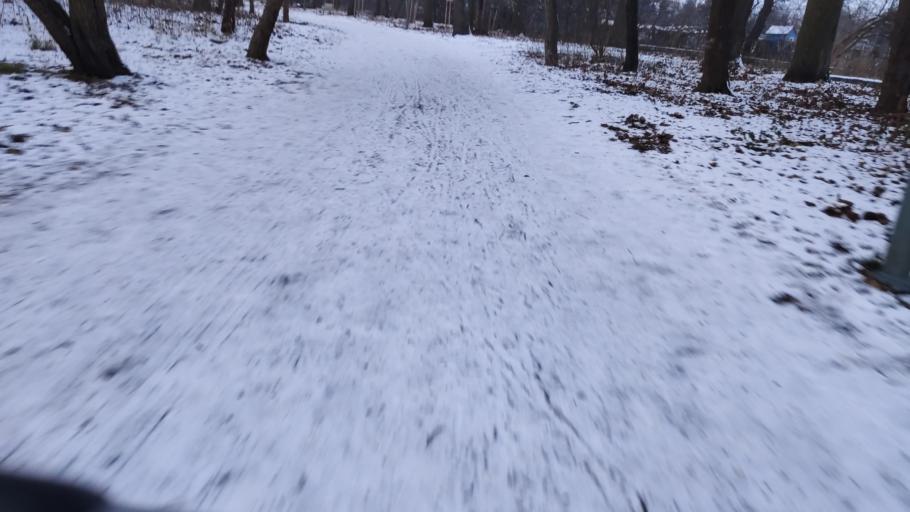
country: PL
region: Lower Silesian Voivodeship
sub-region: Powiat wroclawski
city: Wroclaw
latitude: 51.0851
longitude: 16.9934
